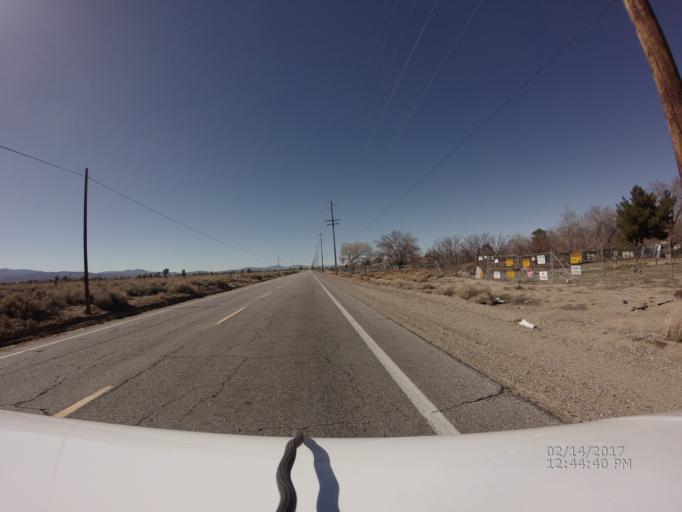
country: US
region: California
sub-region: Los Angeles County
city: Lake Los Angeles
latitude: 34.5800
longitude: -117.8548
